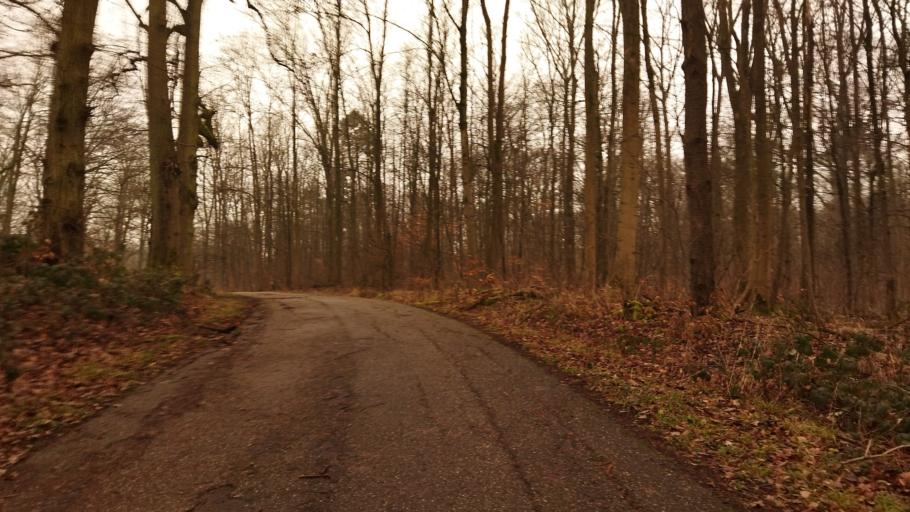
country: DE
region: Baden-Wuerttemberg
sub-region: Regierungsbezirk Stuttgart
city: Weinsberg
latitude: 49.1380
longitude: 9.2770
